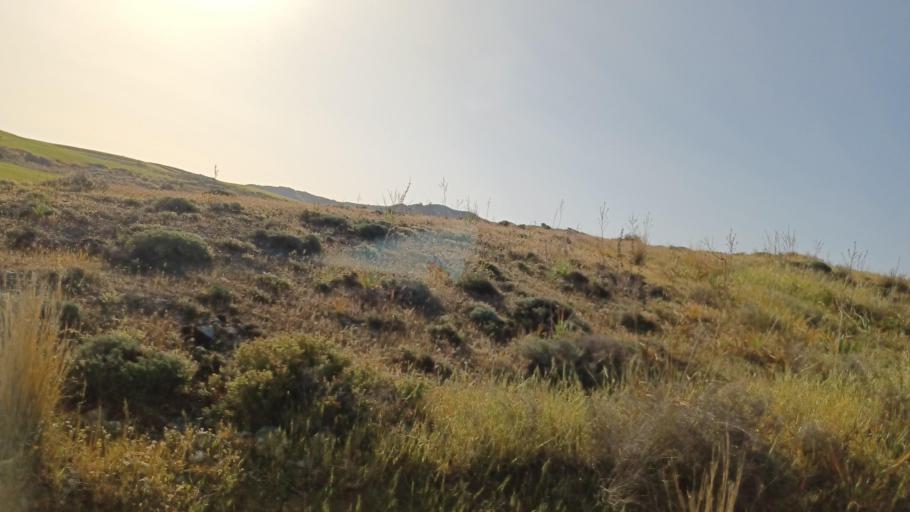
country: CY
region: Lefkosia
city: Astromeritis
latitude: 35.0769
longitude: 33.0276
